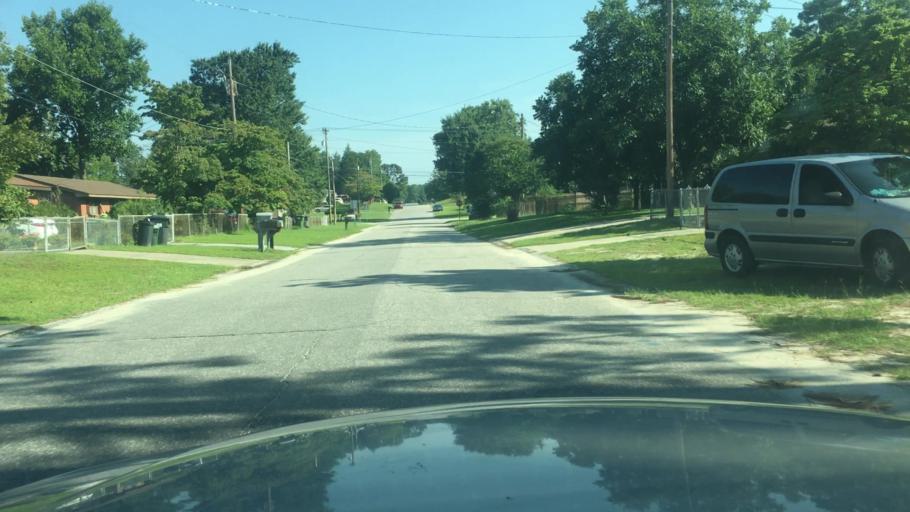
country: US
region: North Carolina
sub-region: Cumberland County
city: Spring Lake
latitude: 35.1524
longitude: -78.9184
